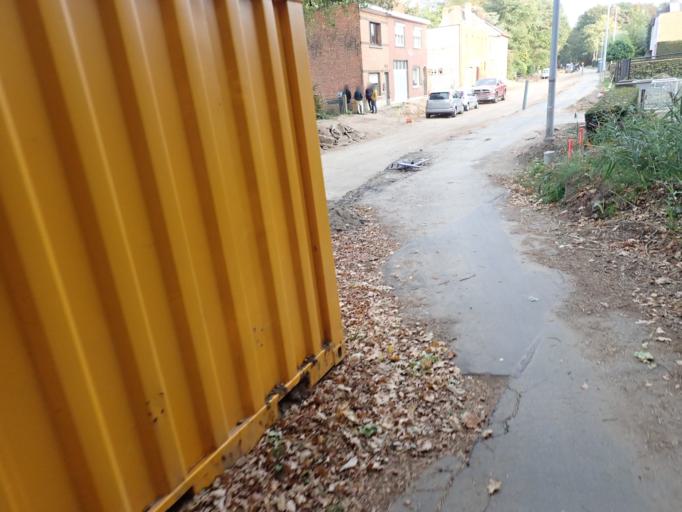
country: BE
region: Flanders
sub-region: Provincie Oost-Vlaanderen
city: Temse
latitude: 51.1766
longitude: 4.1970
